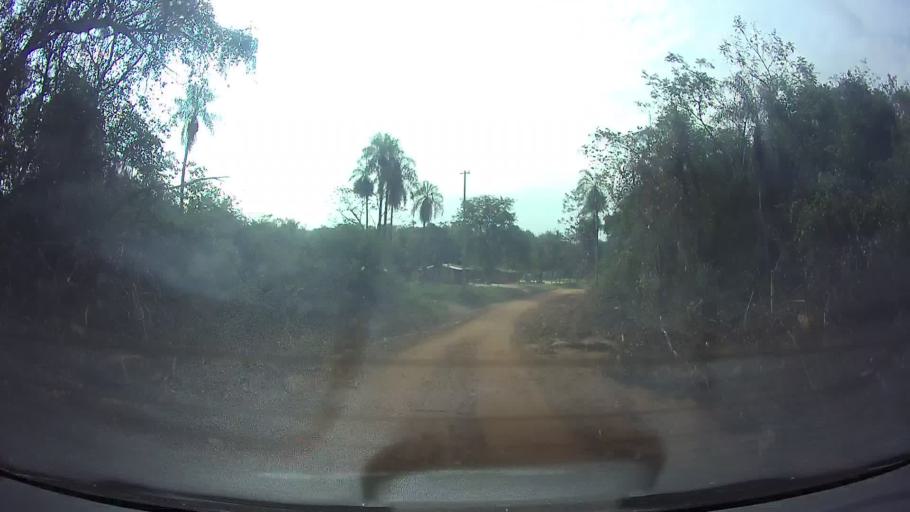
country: PY
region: Cordillera
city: Arroyos y Esteros
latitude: -25.0135
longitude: -57.1982
